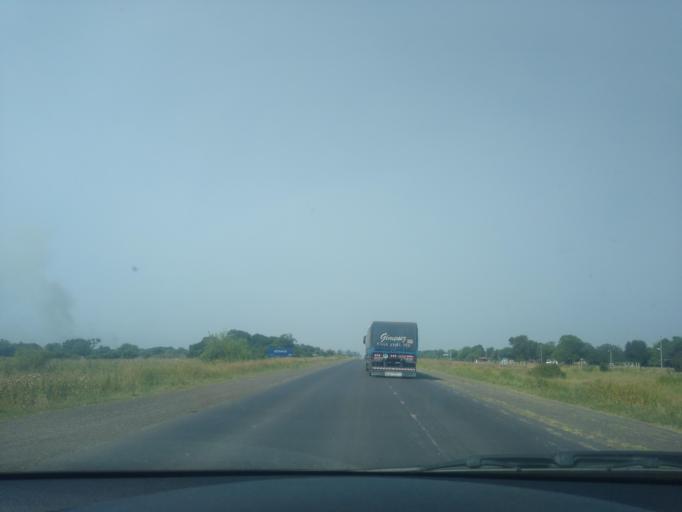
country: AR
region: Chaco
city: Fontana
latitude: -27.4822
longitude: -59.0639
